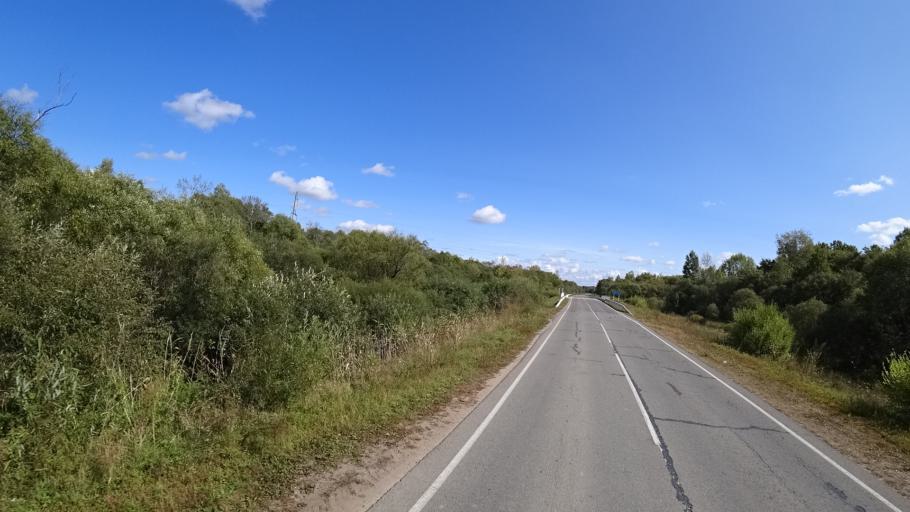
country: RU
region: Amur
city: Arkhara
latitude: 49.4065
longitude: 130.1225
